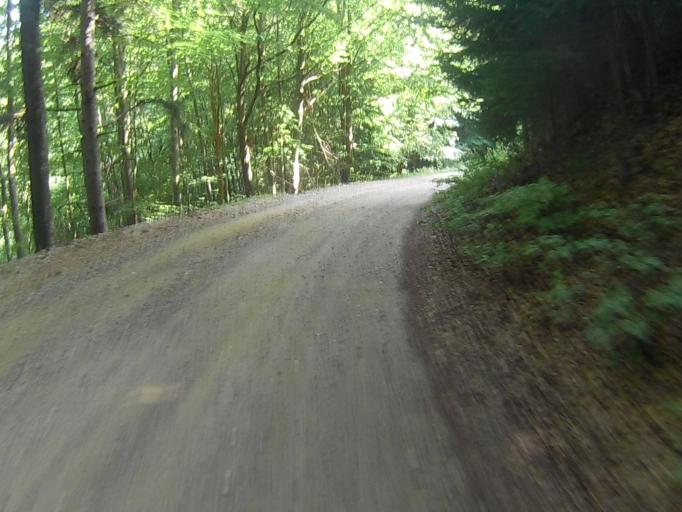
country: SI
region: Maribor
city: Limbus
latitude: 46.5230
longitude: 15.5739
